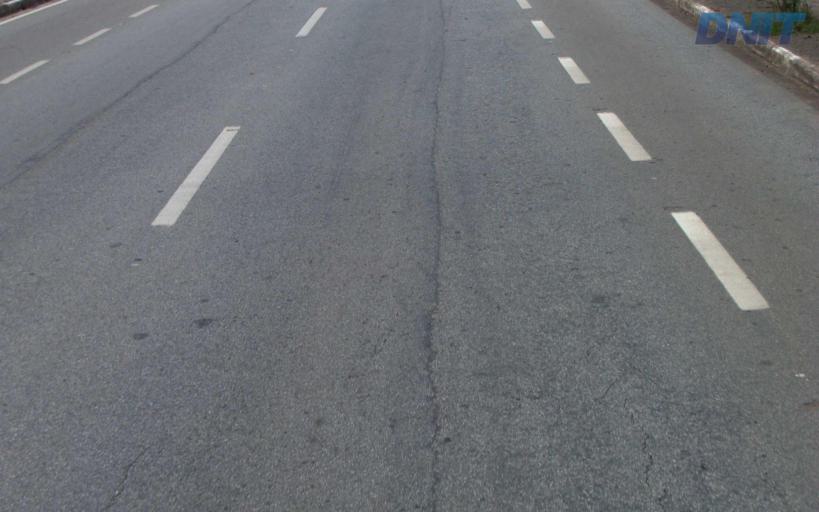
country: BR
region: Minas Gerais
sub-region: Coronel Fabriciano
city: Coronel Fabriciano
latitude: -19.5084
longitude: -42.5799
